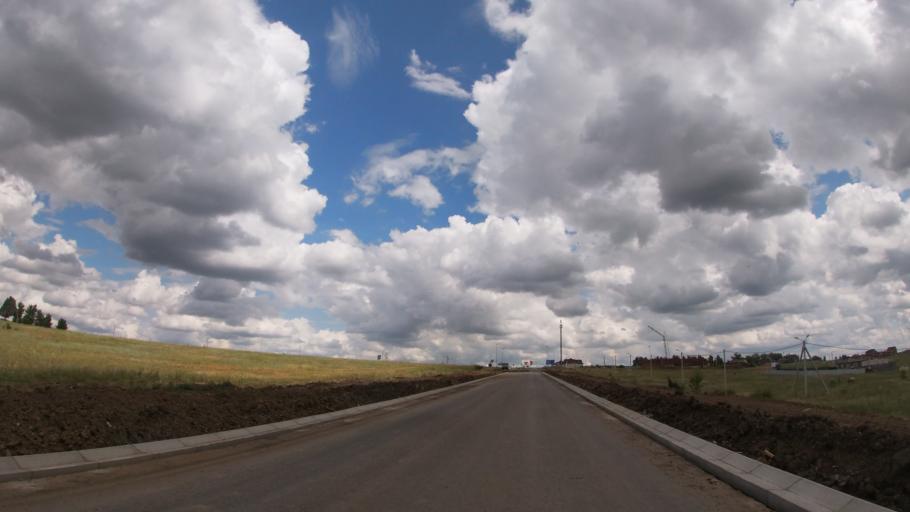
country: RU
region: Belgorod
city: Mayskiy
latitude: 50.5249
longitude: 36.5148
